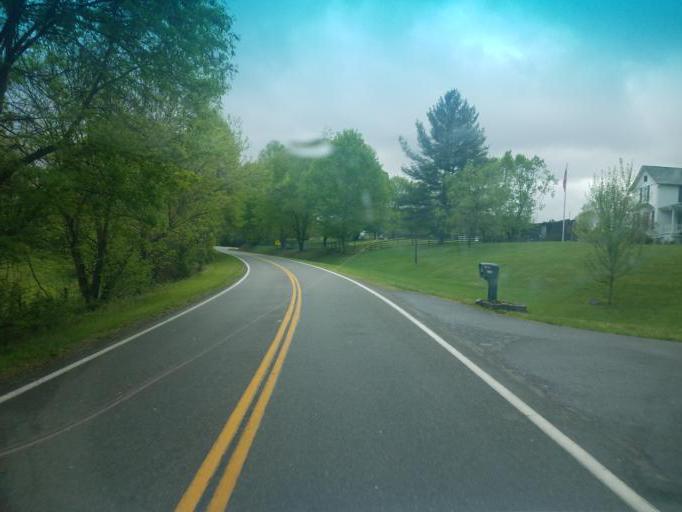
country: US
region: Virginia
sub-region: Washington County
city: Emory
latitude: 36.6560
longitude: -81.7993
